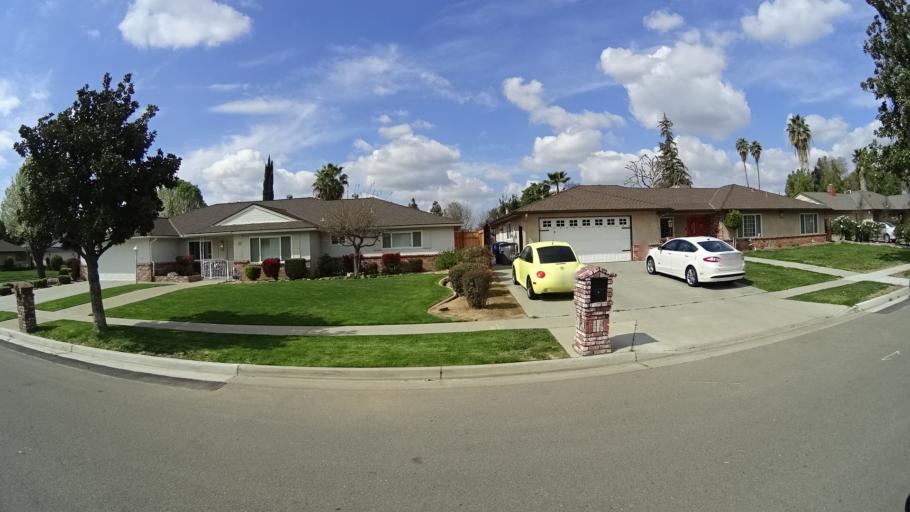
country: US
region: California
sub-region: Fresno County
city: Fresno
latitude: 36.8166
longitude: -119.8484
